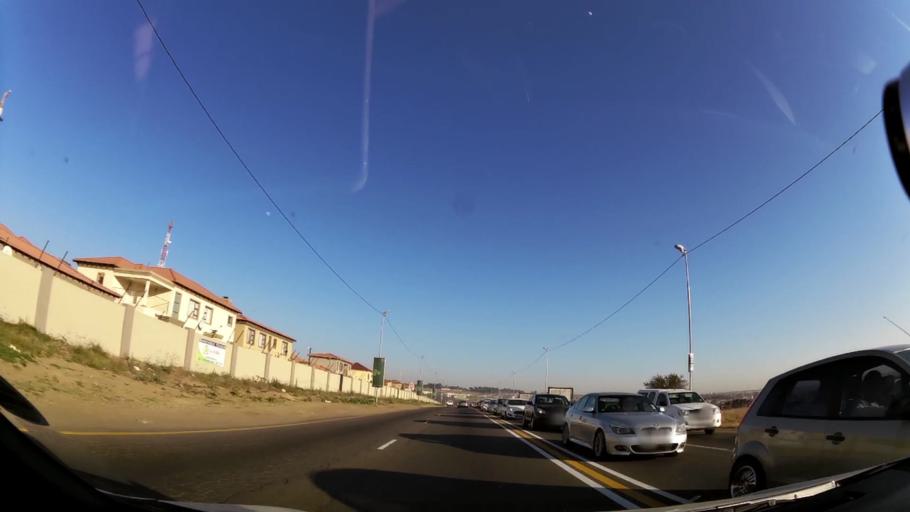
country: ZA
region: Gauteng
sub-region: City of Johannesburg Metropolitan Municipality
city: Midrand
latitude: -25.9489
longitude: 28.1192
